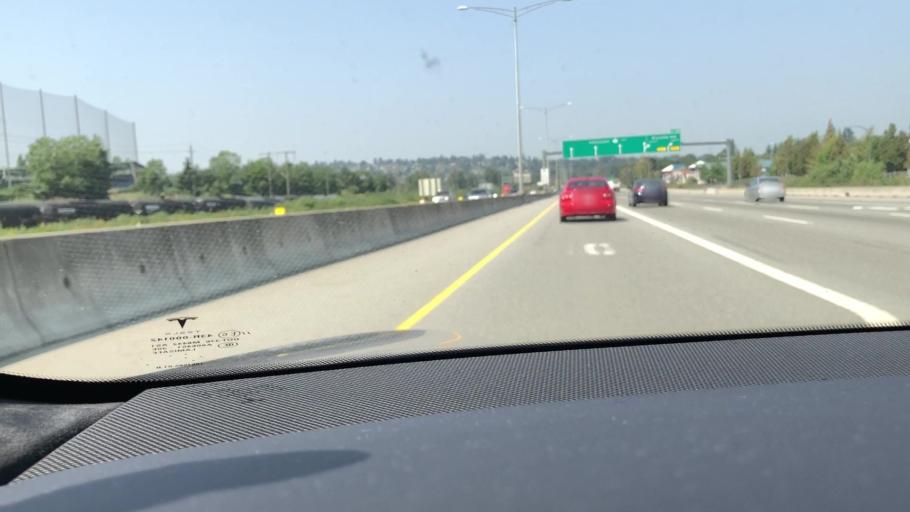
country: CA
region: British Columbia
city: Port Moody
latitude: 49.2327
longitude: -122.8647
